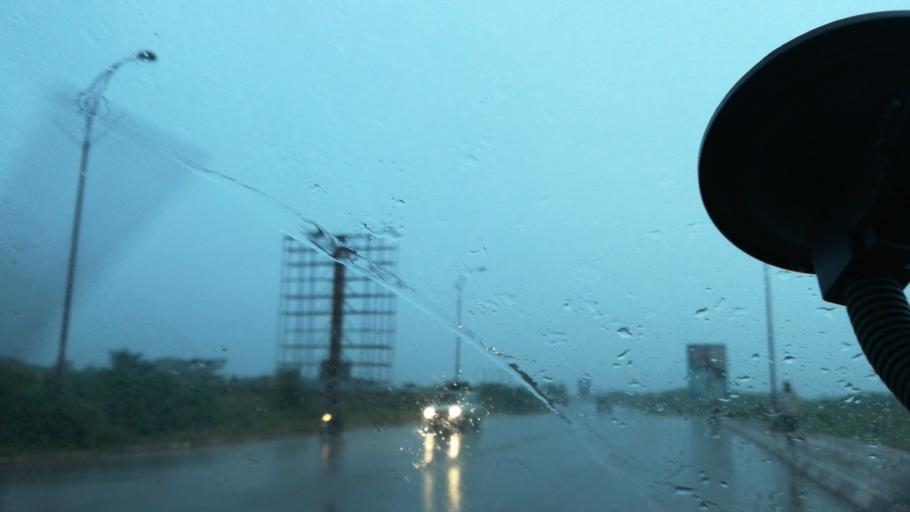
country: CD
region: Katanga
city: Lubumbashi
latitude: -11.5978
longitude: 27.4973
